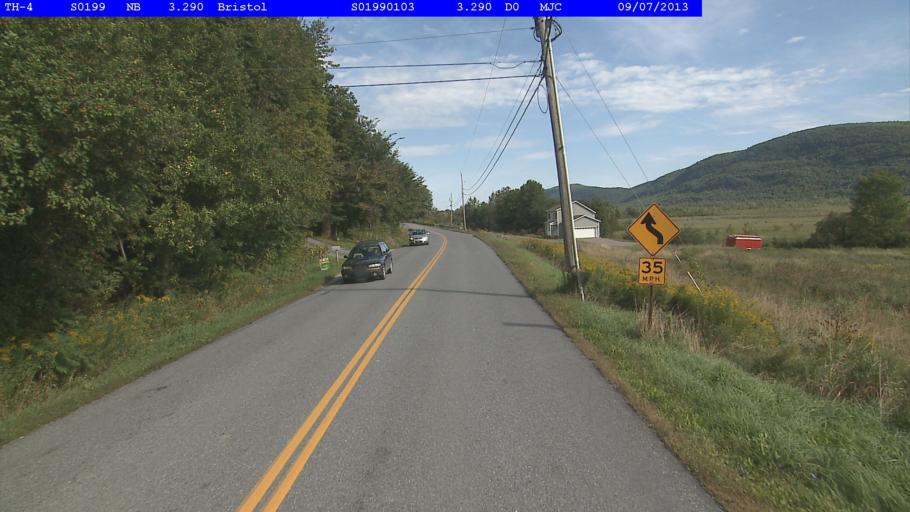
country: US
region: Vermont
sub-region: Addison County
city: Bristol
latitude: 44.1756
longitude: -73.1023
